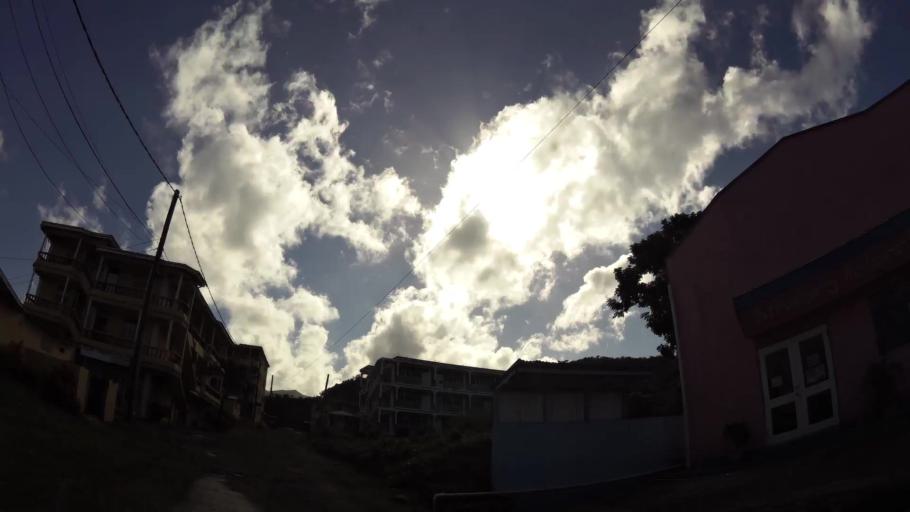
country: DM
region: Saint John
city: Portsmouth
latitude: 15.5540
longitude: -61.4599
